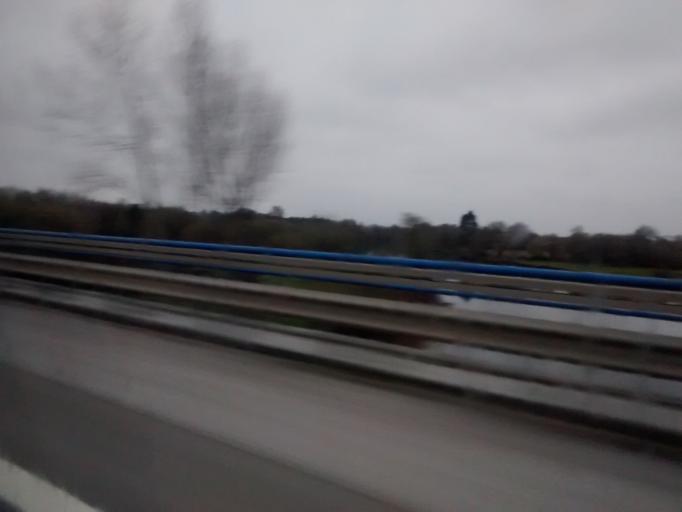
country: PT
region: Aveiro
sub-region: Aveiro
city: Eixo
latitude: 40.6776
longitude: -8.5715
